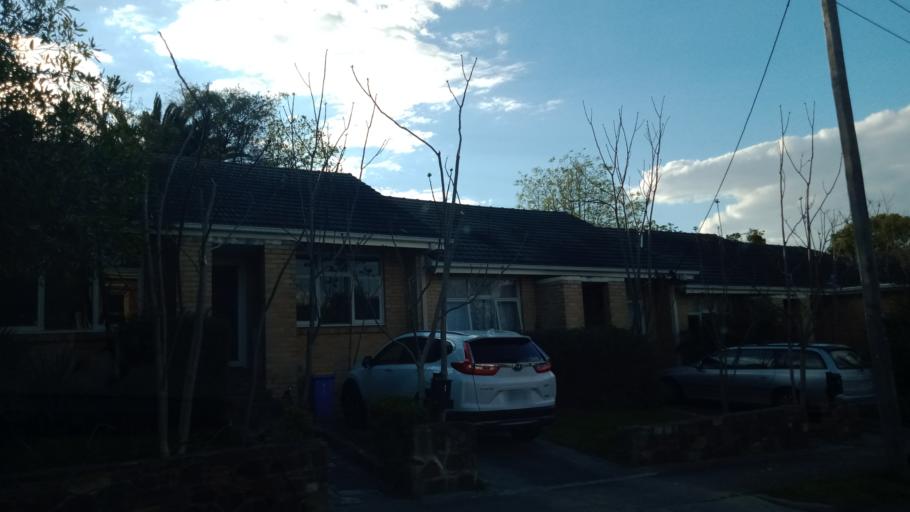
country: AU
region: Victoria
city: Glenferrie
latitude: -37.8361
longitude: 145.0584
